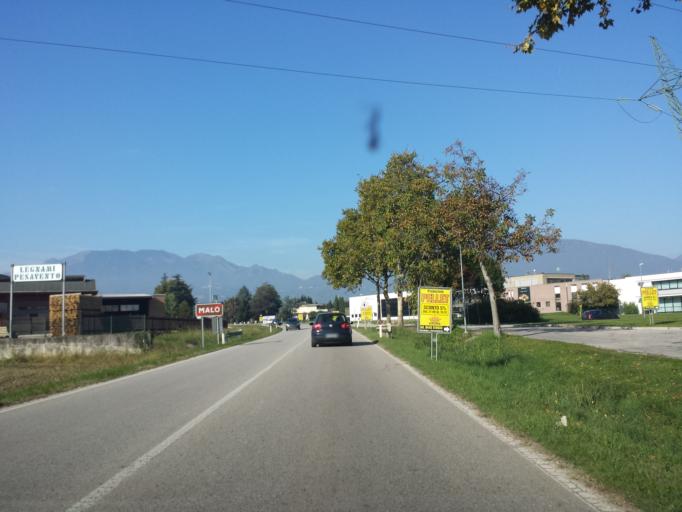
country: IT
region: Veneto
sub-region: Provincia di Vicenza
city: San Vito di Leguzzano
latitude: 45.6844
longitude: 11.3995
